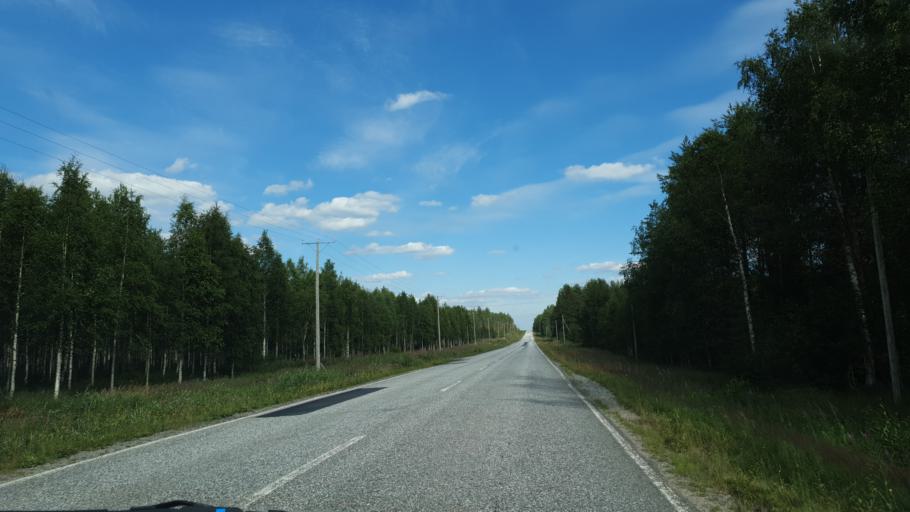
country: FI
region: Kainuu
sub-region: Kajaani
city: Sotkamo
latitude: 64.1555
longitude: 28.6604
